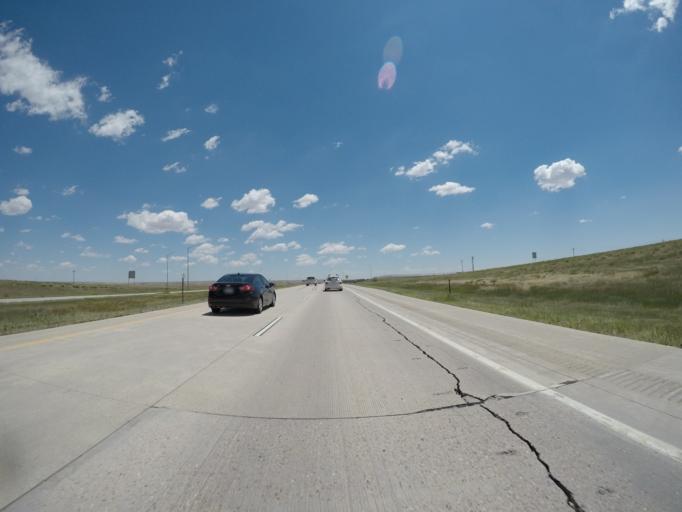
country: US
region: Colorado
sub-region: Lincoln County
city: Limon
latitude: 39.2732
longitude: -103.7058
